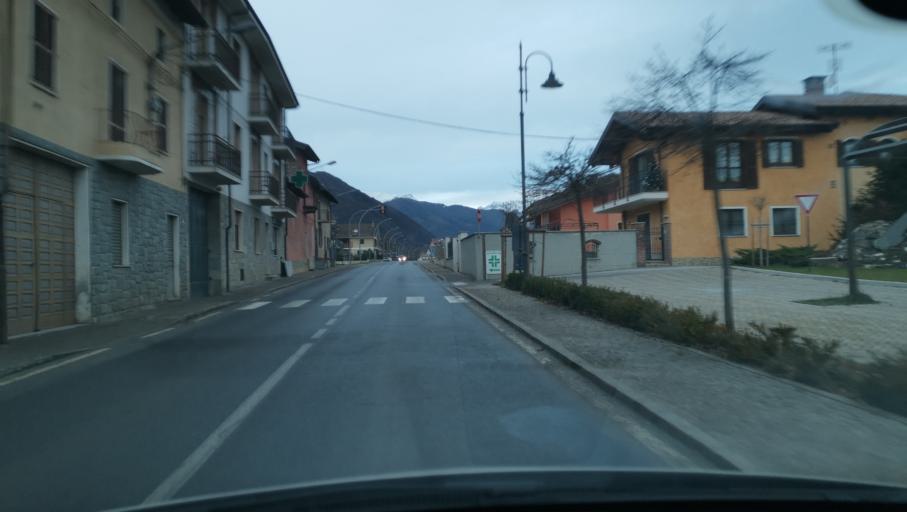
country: IT
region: Piedmont
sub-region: Provincia di Cuneo
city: Valgrana
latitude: 44.4124
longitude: 7.3802
